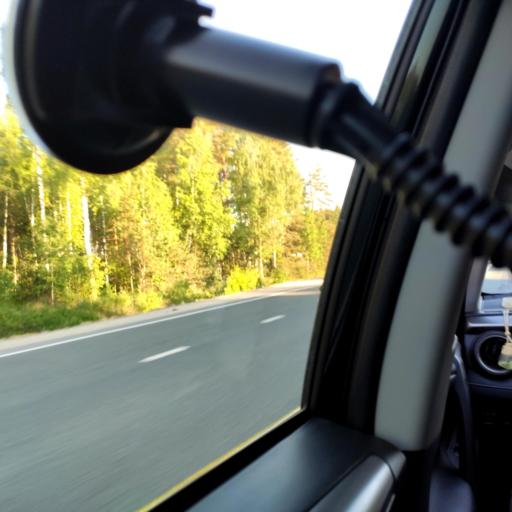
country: RU
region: Mariy-El
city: Suslonger
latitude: 56.2428
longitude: 48.2317
